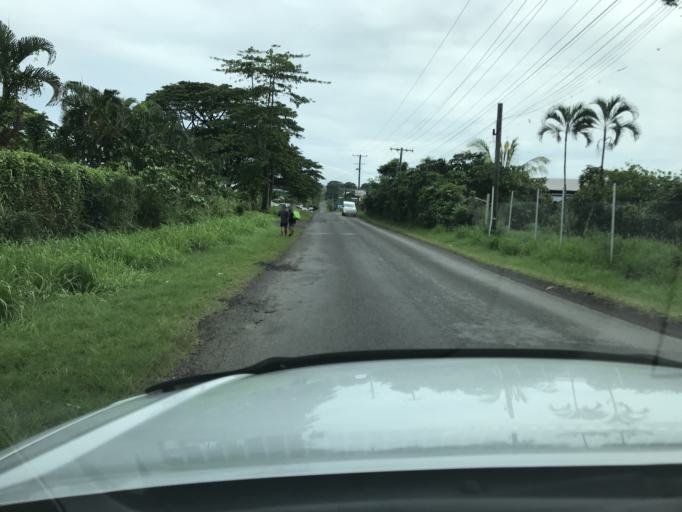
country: WS
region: Tuamasaga
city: Vaiusu
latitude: -13.8234
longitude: -171.8067
